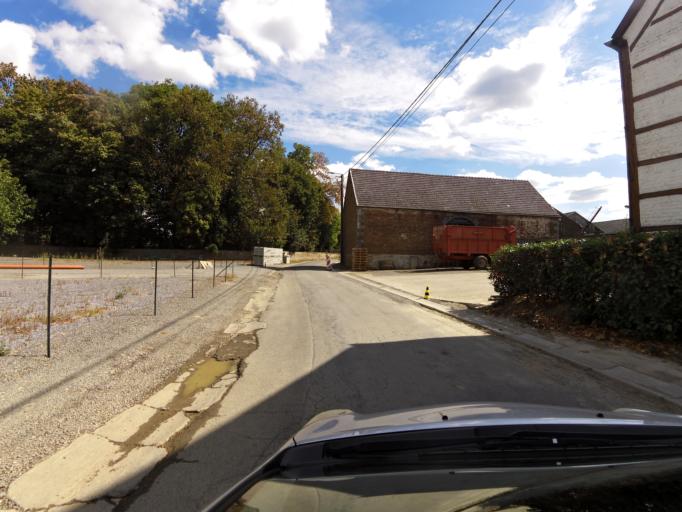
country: BE
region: Wallonia
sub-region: Province de Namur
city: Somme-Leuze
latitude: 50.3293
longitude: 5.4095
